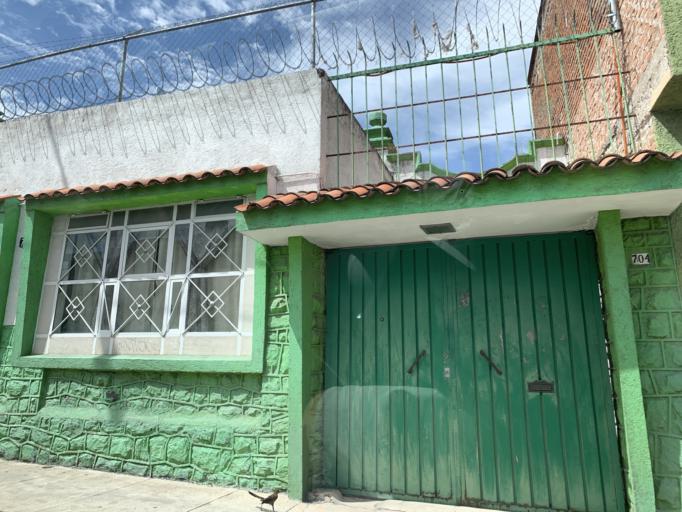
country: MX
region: Puebla
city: Puebla
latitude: 19.0616
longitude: -98.1950
